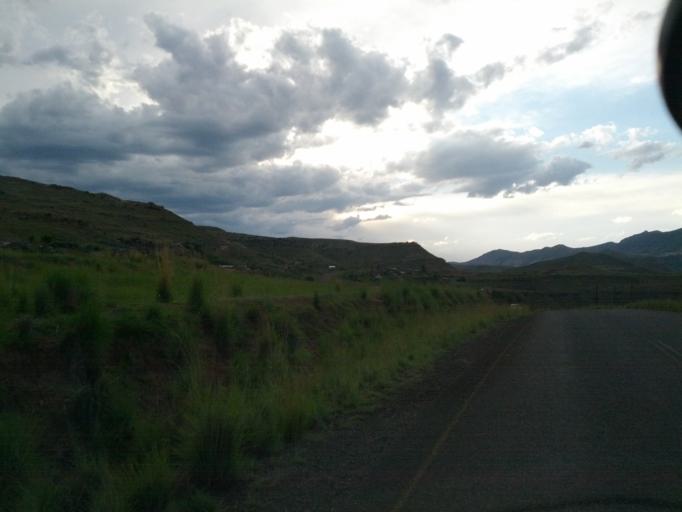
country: LS
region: Qacha's Nek
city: Qacha's Nek
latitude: -30.0667
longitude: 28.5466
